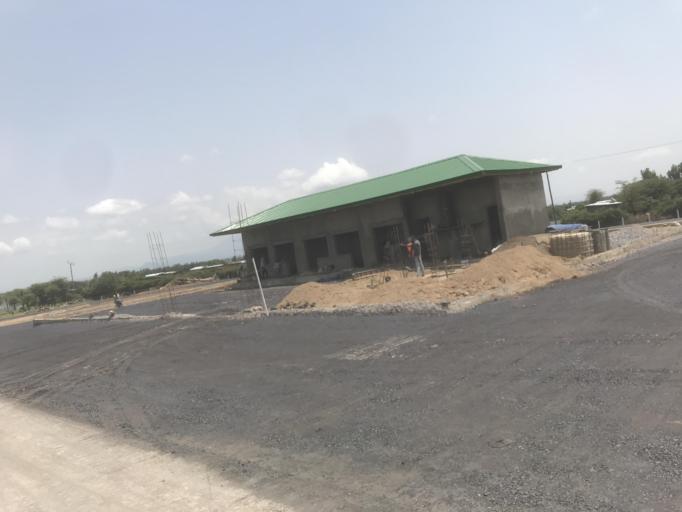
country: ET
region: Oromiya
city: Mojo
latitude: 8.3008
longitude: 38.9402
